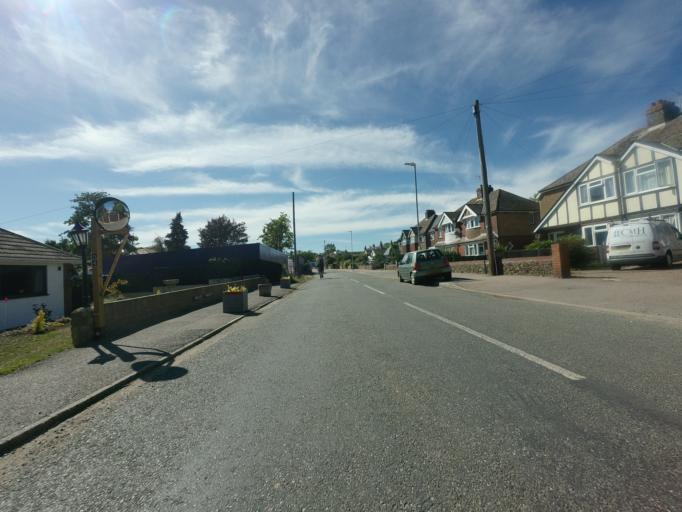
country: GB
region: England
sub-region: Kent
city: Birchington-on-Sea
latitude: 51.3352
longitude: 1.3079
